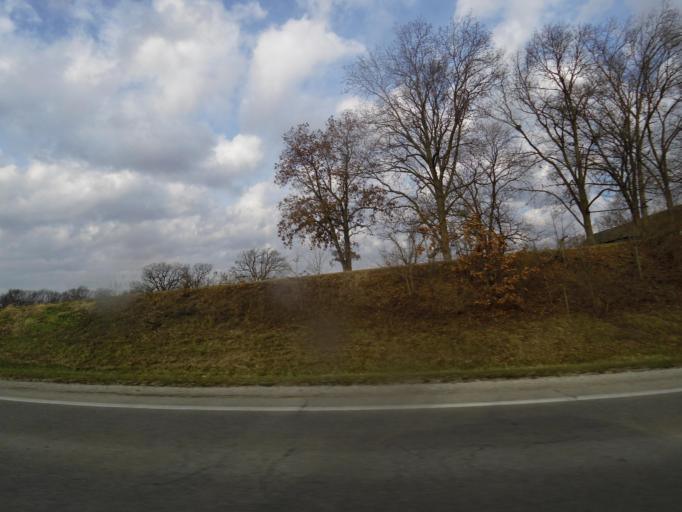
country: US
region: Illinois
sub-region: Christian County
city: Pana
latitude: 39.3021
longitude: -89.0877
